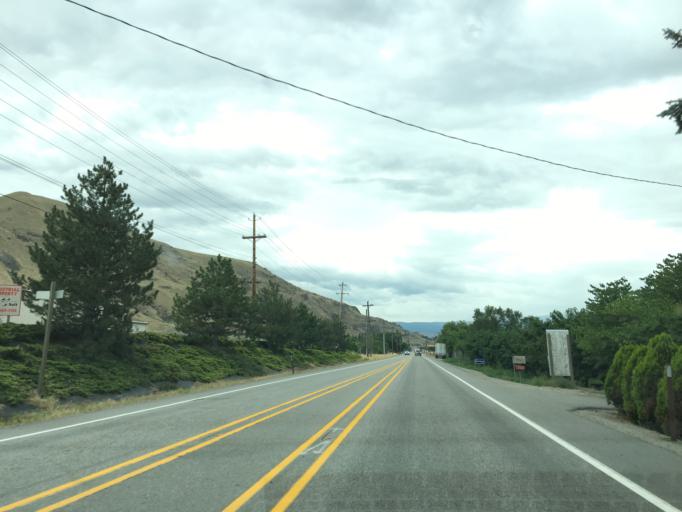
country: US
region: Washington
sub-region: Chelan County
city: Sunnyslope
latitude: 47.5092
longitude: -120.2973
